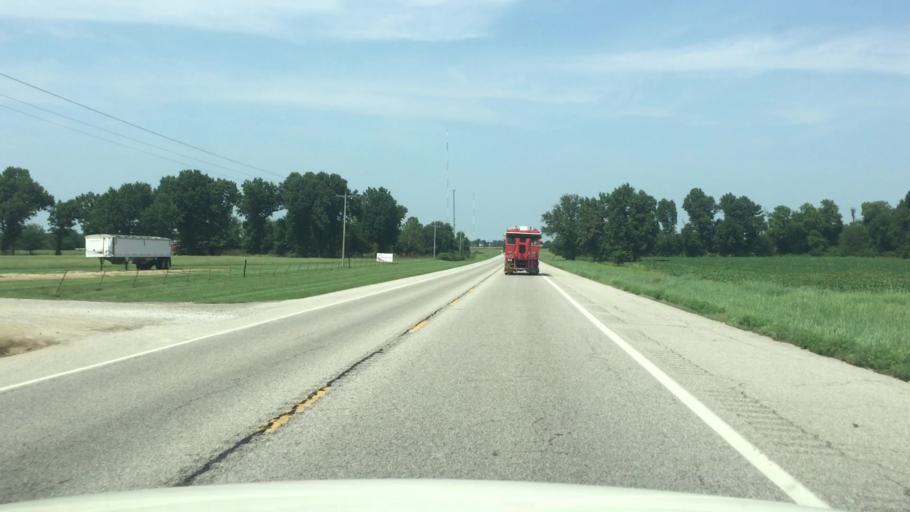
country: US
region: Kansas
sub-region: Cherokee County
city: Galena
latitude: 37.1971
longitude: -94.7046
